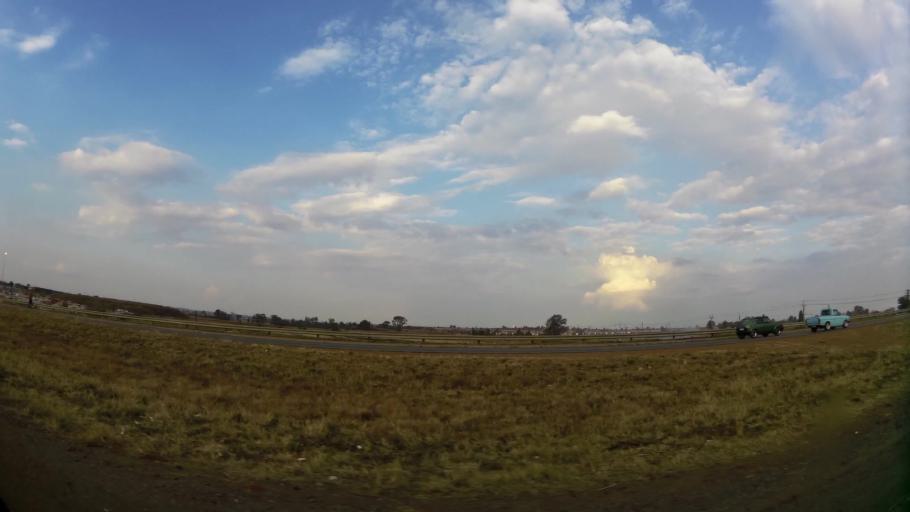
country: ZA
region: Gauteng
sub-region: Sedibeng District Municipality
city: Vanderbijlpark
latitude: -26.6056
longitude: 27.8169
